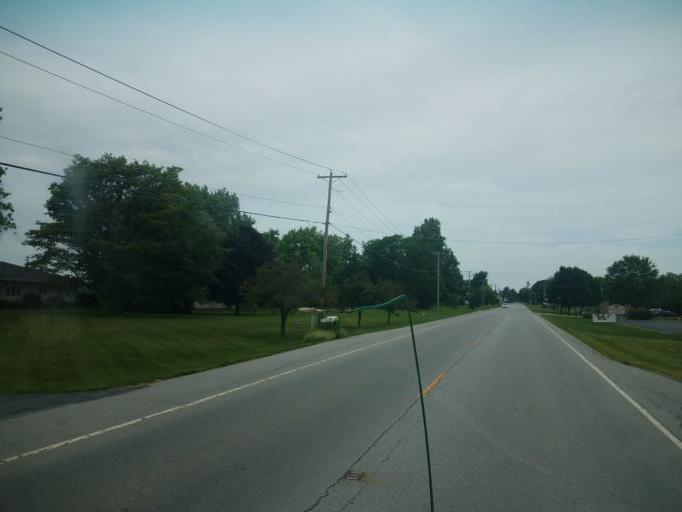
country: US
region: Ohio
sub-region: Hardin County
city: Ada
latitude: 40.7554
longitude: -83.8232
